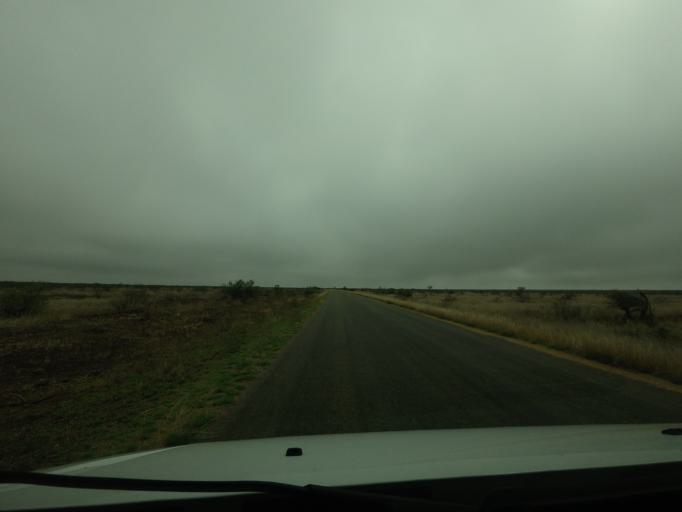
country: ZA
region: Limpopo
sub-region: Mopani District Municipality
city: Phalaborwa
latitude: -24.2434
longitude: 31.7210
